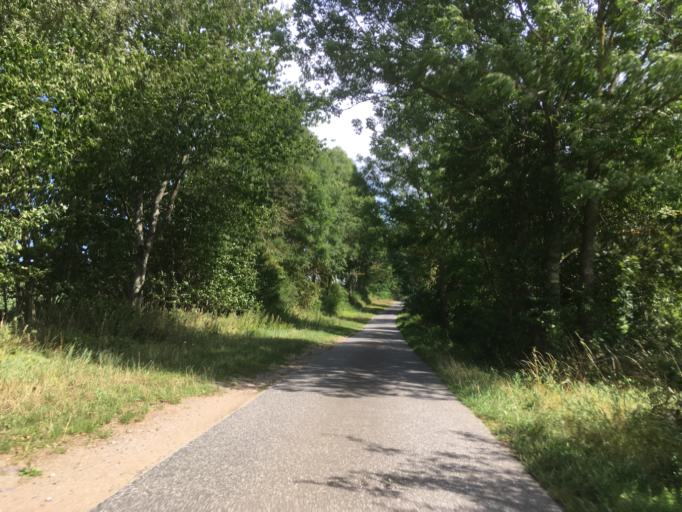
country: DE
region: Brandenburg
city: Gerswalde
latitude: 53.1264
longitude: 13.8277
